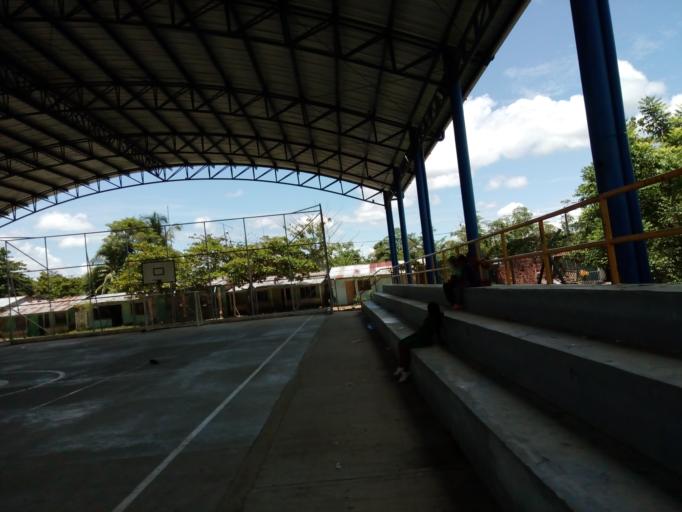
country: CO
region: Boyaca
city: Puerto Boyaca
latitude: 6.0667
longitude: -74.2675
